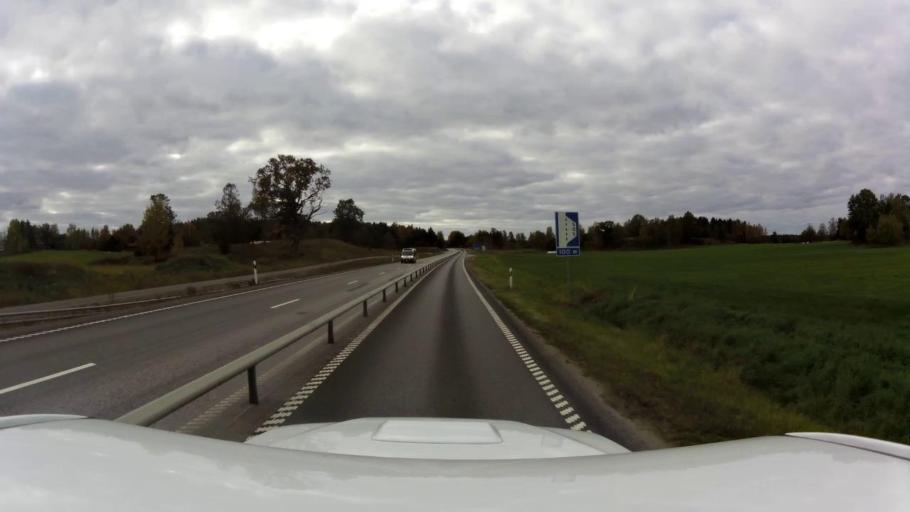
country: SE
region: OEstergoetland
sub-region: Linkopings Kommun
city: Malmslatt
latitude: 58.3077
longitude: 15.5660
